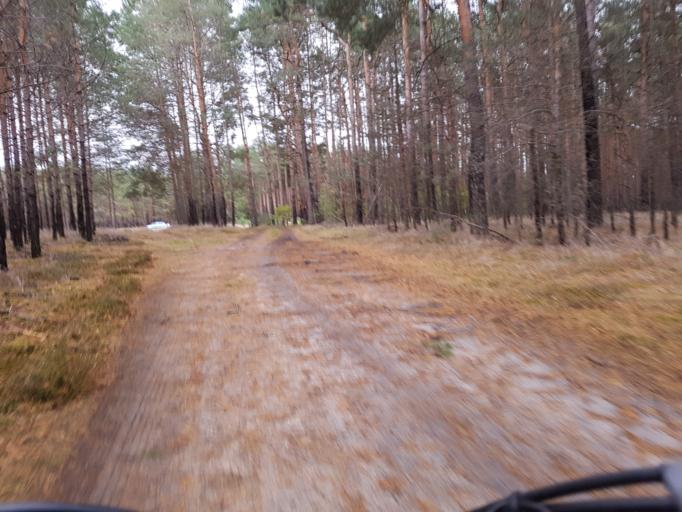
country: DE
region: Brandenburg
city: Schilda
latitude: 51.6222
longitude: 13.3673
